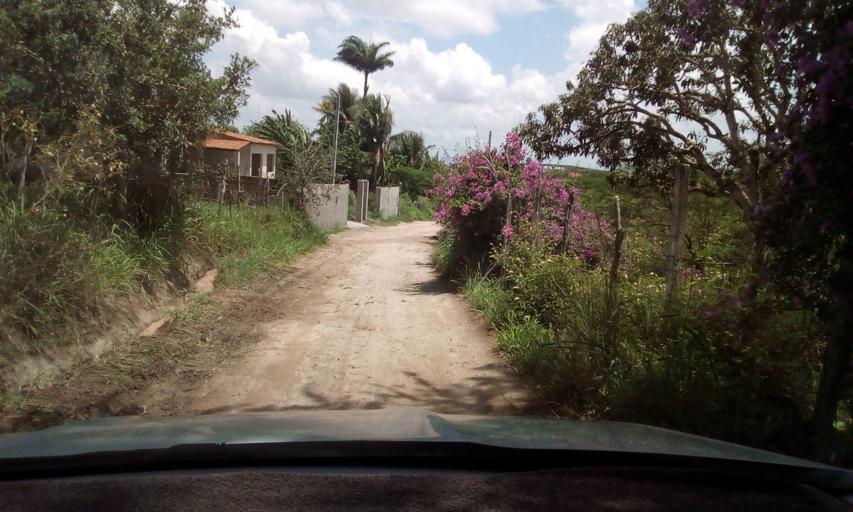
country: BR
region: Pernambuco
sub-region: Cha Grande
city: Cha Grande
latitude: -8.1912
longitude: -35.4973
